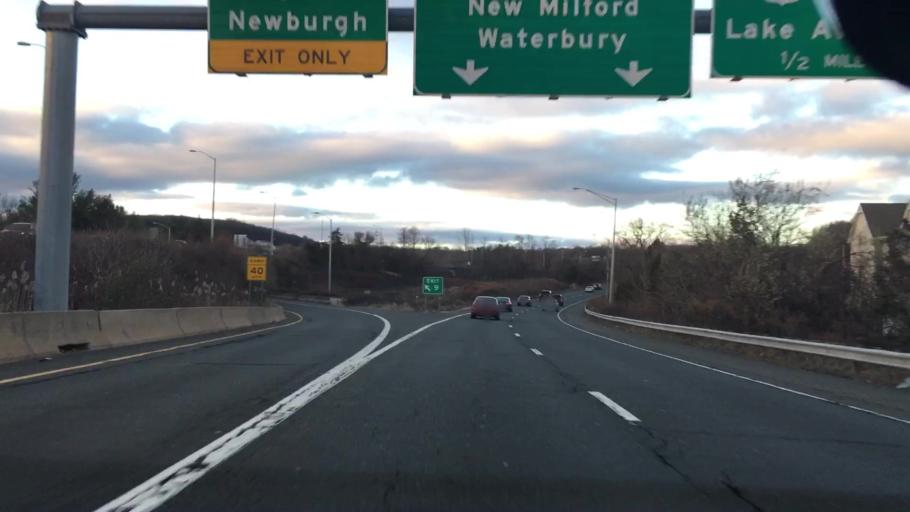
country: US
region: Connecticut
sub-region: Fairfield County
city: Danbury
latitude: 41.3829
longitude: -73.4754
